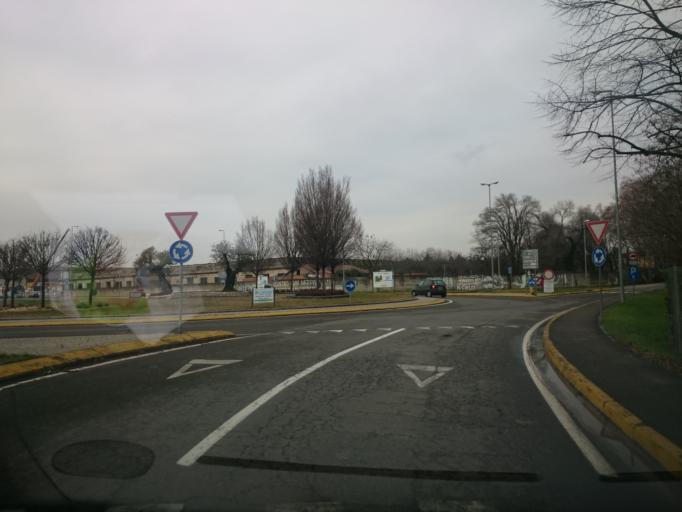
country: IT
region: Emilia-Romagna
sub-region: Provincia di Reggio Emilia
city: Reggio nell'Emilia
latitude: 44.7002
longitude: 10.6538
